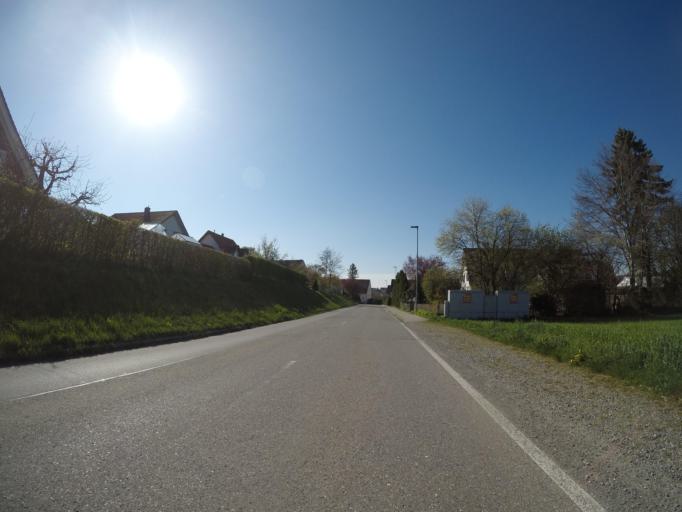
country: DE
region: Baden-Wuerttemberg
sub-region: Tuebingen Region
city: Ebenweiler
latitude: 47.9043
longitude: 9.5117
